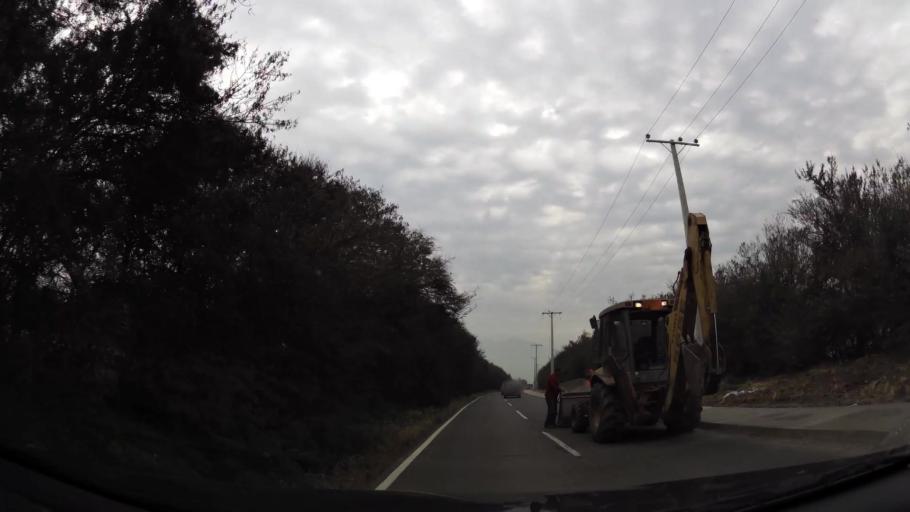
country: CL
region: Santiago Metropolitan
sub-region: Provincia de Chacabuco
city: Chicureo Abajo
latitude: -33.2310
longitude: -70.6895
